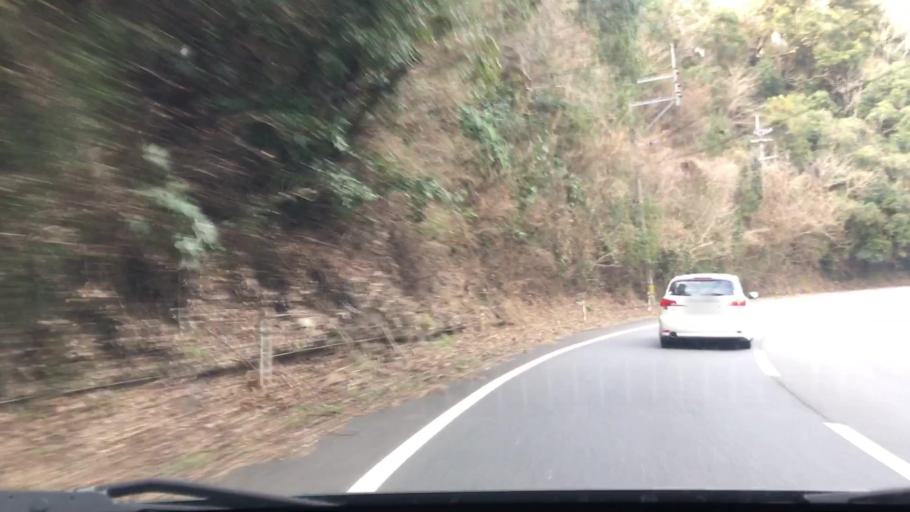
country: JP
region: Miyazaki
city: Nichinan
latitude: 31.7477
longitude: 131.3340
